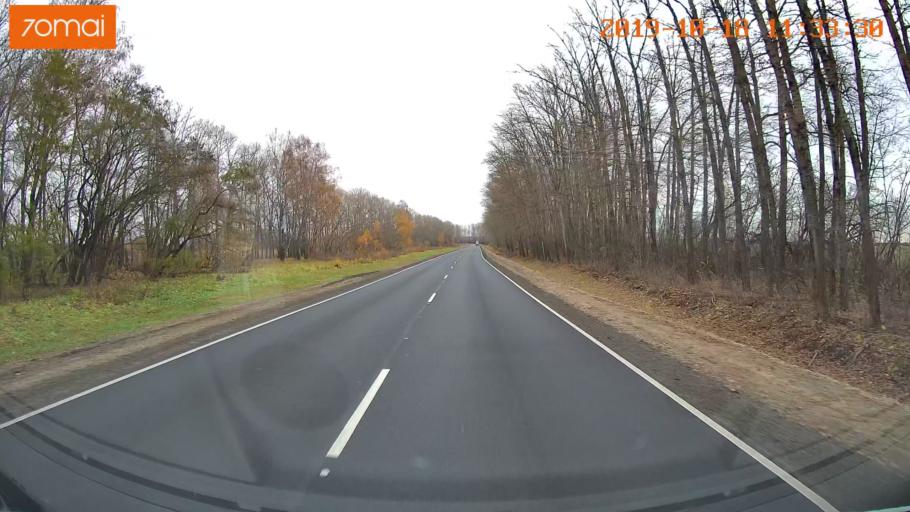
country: RU
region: Rjazan
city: Oktyabr'skiy
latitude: 54.1407
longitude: 38.7418
